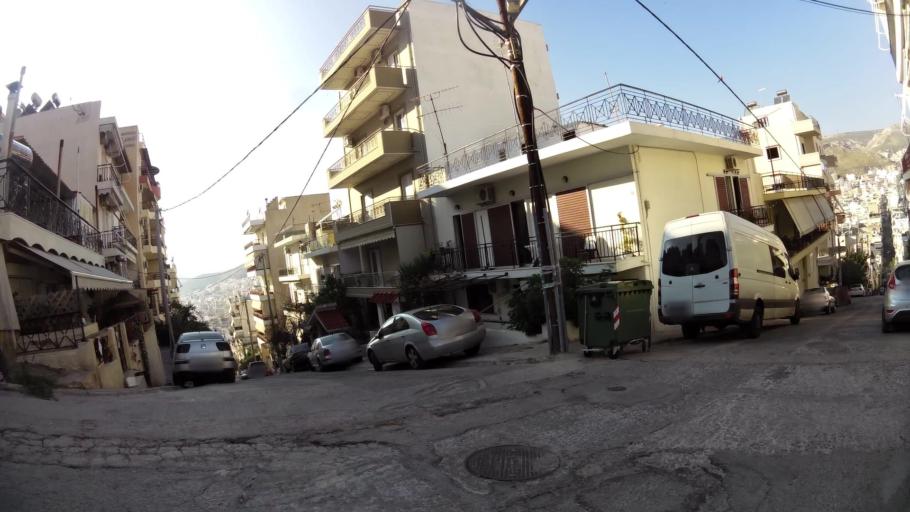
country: GR
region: Attica
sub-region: Nomos Piraios
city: Keratsini
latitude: 37.9725
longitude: 23.6308
